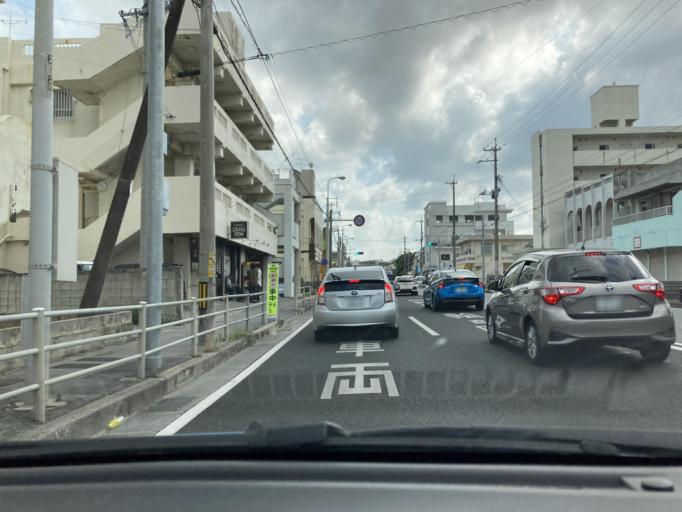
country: JP
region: Okinawa
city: Ginowan
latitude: 26.2061
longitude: 127.7563
